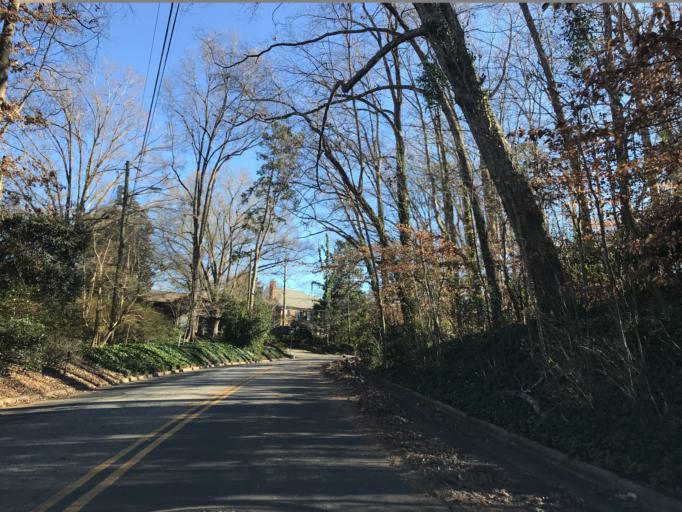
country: US
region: North Carolina
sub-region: Wake County
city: West Raleigh
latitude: 35.8195
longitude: -78.6435
